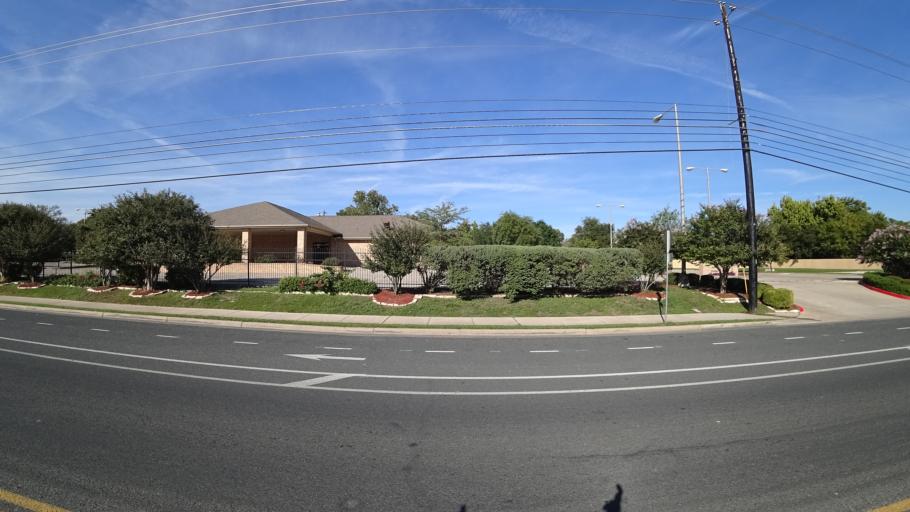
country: US
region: Texas
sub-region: Travis County
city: Austin
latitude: 30.2553
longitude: -97.6838
